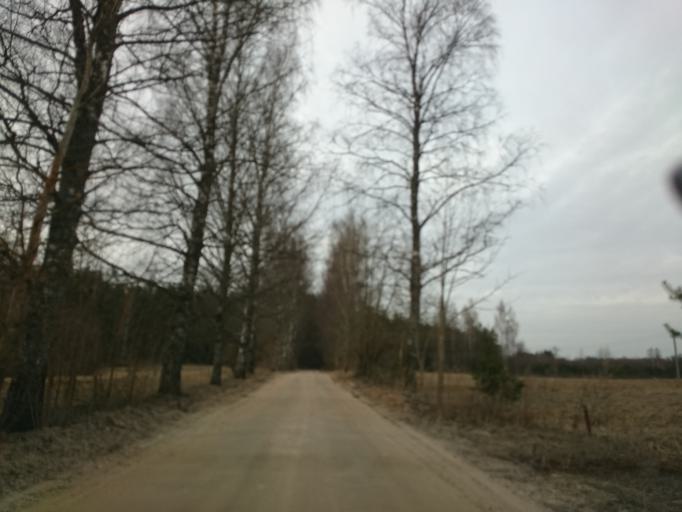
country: LV
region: Garkalne
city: Garkalne
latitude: 57.0170
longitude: 24.3869
